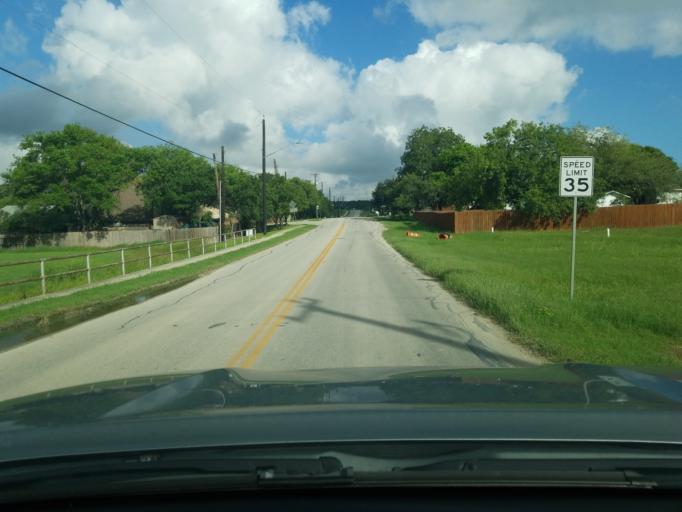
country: US
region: Texas
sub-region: Bexar County
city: Live Oak
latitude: 29.5780
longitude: -98.3619
